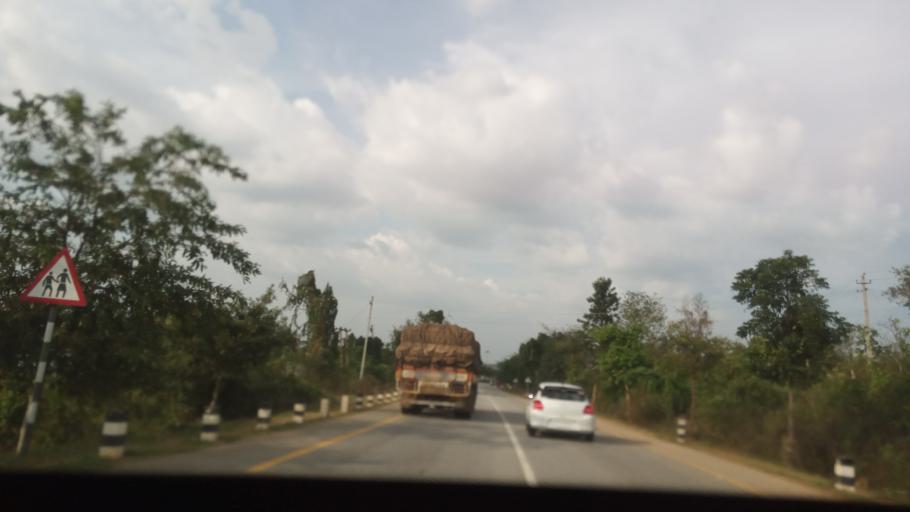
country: IN
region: Karnataka
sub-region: Tumkur
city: Kunigal
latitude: 12.8717
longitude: 77.0408
